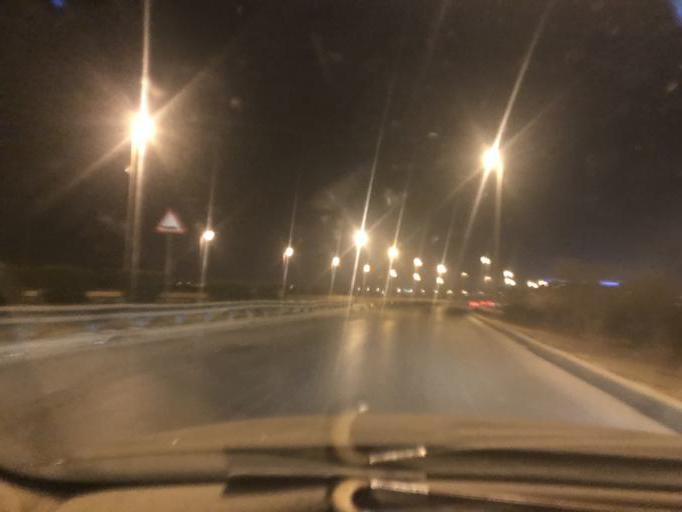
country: SA
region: Ar Riyad
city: Riyadh
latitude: 24.8257
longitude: 46.7164
